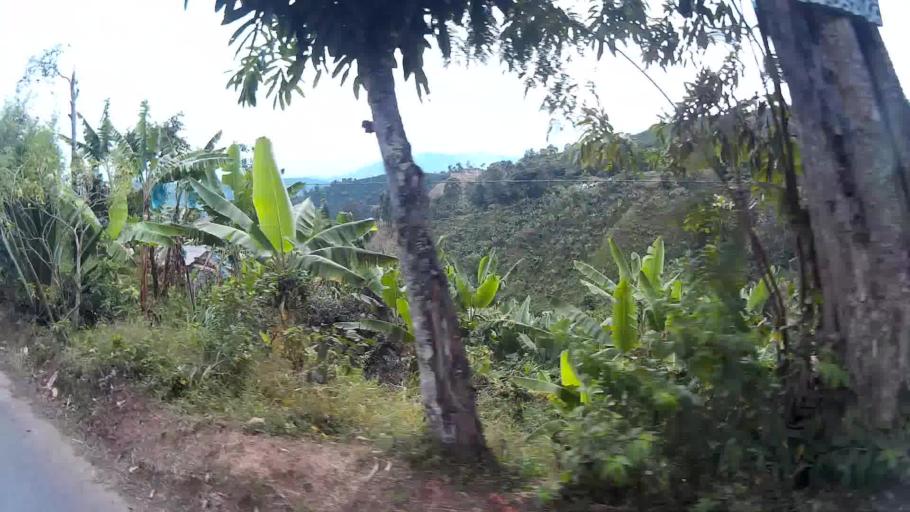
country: CO
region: Risaralda
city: Marsella
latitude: 4.9119
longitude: -75.7370
